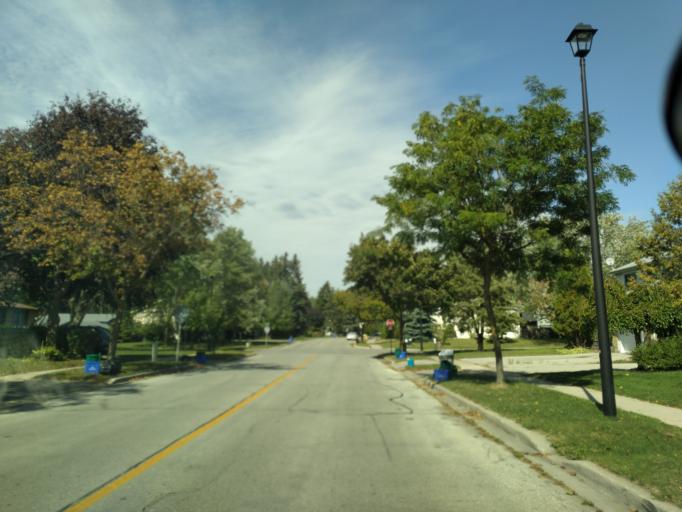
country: CA
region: Ontario
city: Newmarket
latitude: 44.0712
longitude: -79.4423
